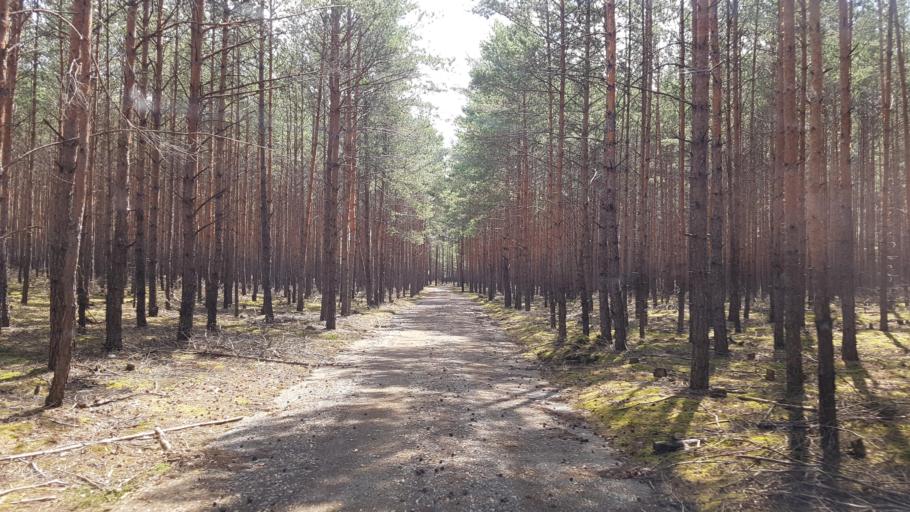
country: DE
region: Brandenburg
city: Crinitz
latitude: 51.6976
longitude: 13.8232
